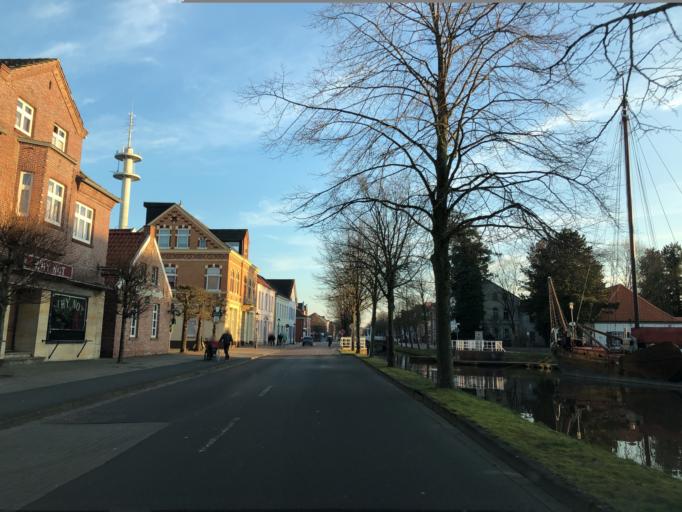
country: DE
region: Lower Saxony
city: Papenburg
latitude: 53.0863
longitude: 7.3888
